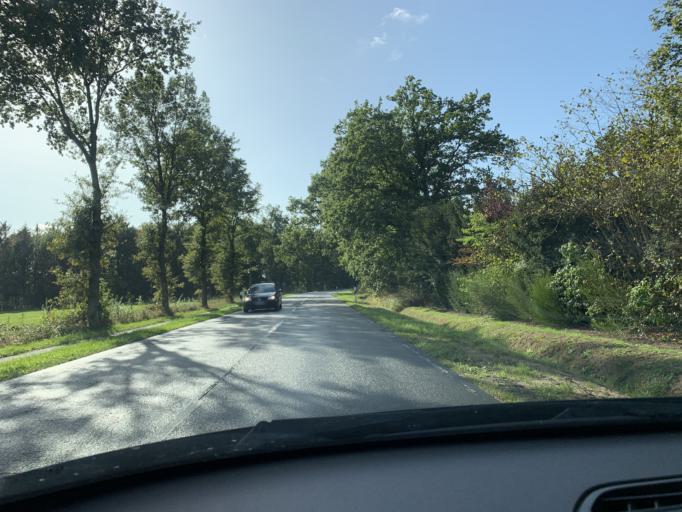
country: DE
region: Lower Saxony
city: Bad Zwischenahn
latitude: 53.1828
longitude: 7.9346
